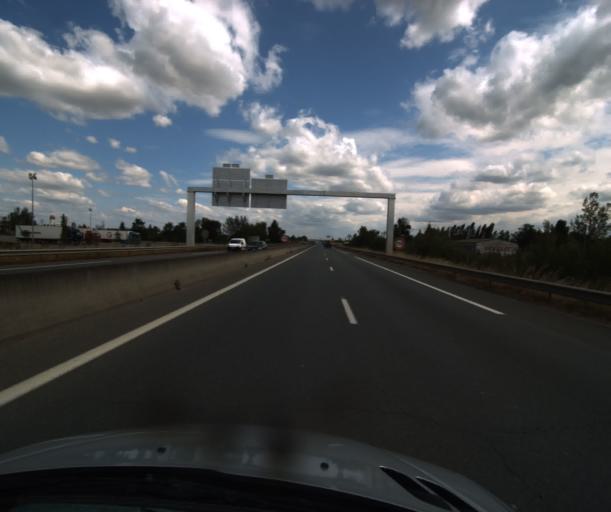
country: FR
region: Midi-Pyrenees
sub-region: Departement du Tarn-et-Garonne
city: Campsas
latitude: 43.9335
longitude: 1.3197
